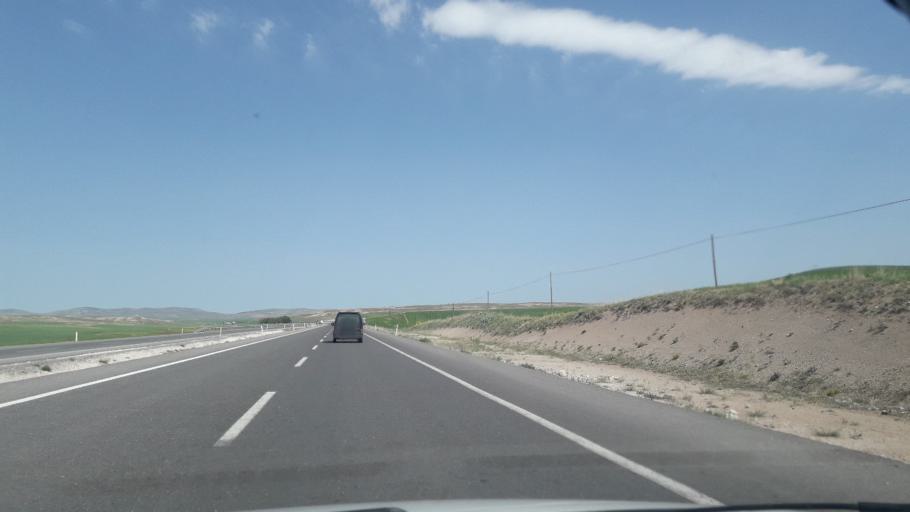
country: TR
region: Sivas
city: Deliktas
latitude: 39.2204
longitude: 37.1934
